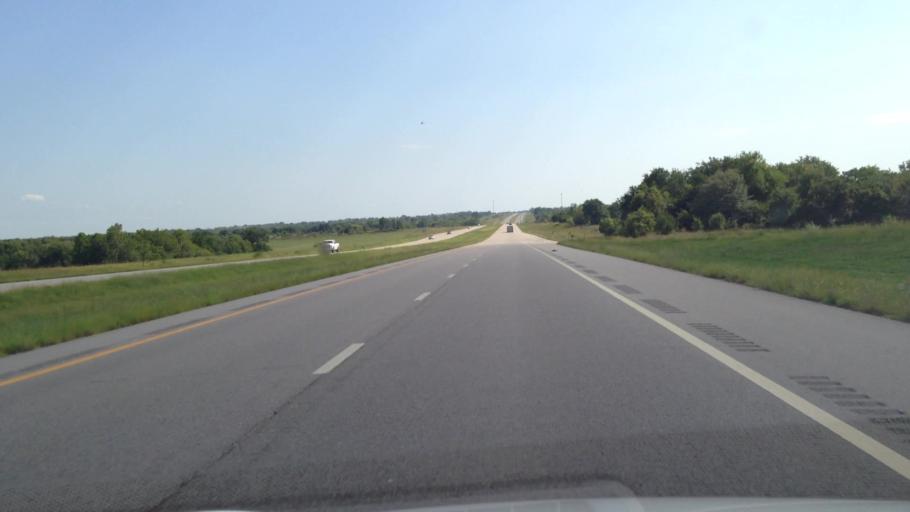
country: US
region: Kansas
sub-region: Linn County
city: La Cygne
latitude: 38.4021
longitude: -94.6882
